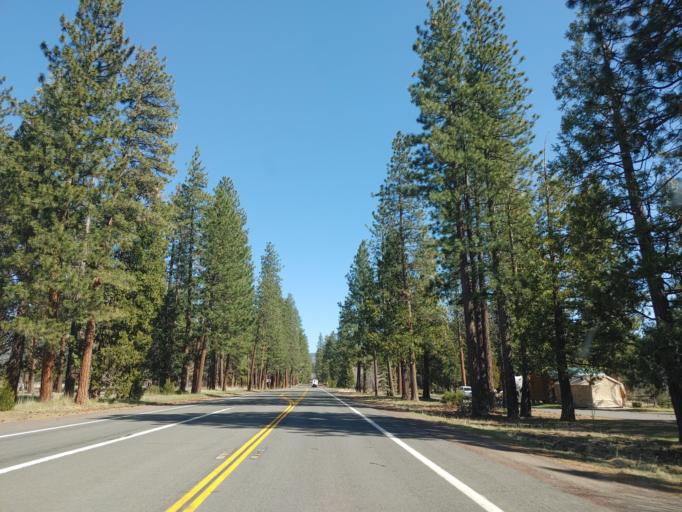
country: US
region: California
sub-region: Shasta County
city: Burney
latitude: 40.7413
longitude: -121.4691
